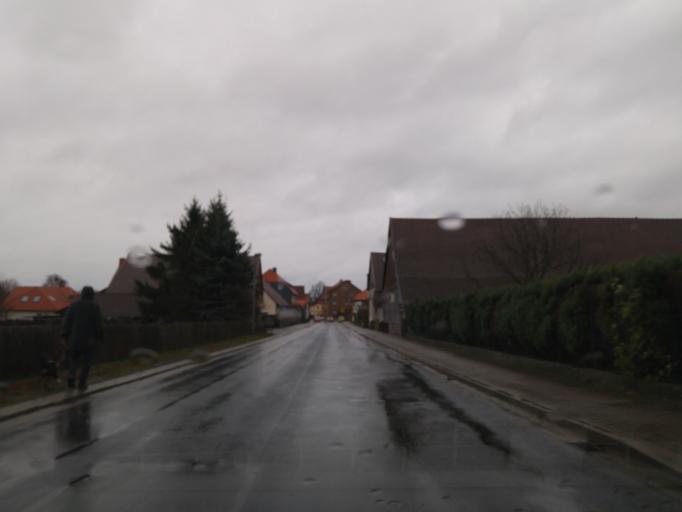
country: DE
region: Lower Saxony
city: Gemeinde Friedland
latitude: 51.4340
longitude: 9.9298
